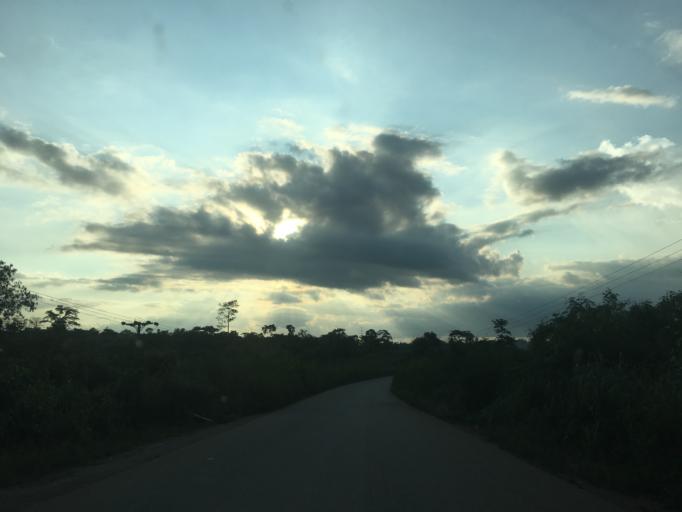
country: GH
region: Western
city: Bibiani
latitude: 6.6333
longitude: -2.4219
